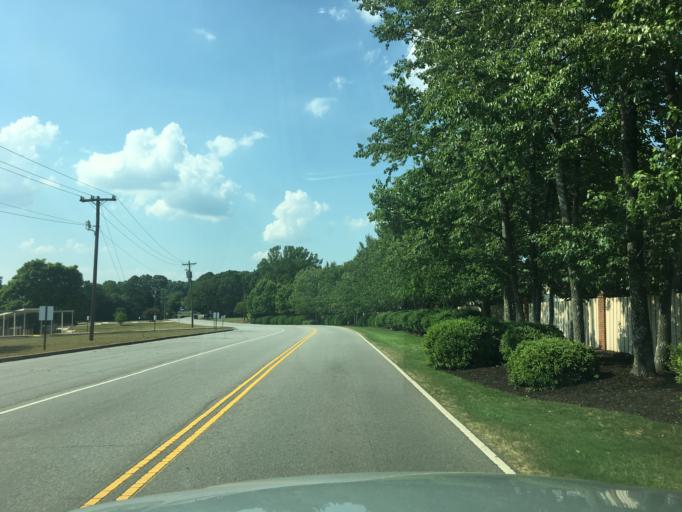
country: US
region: South Carolina
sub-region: Anderson County
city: Anderson
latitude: 34.5296
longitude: -82.6293
